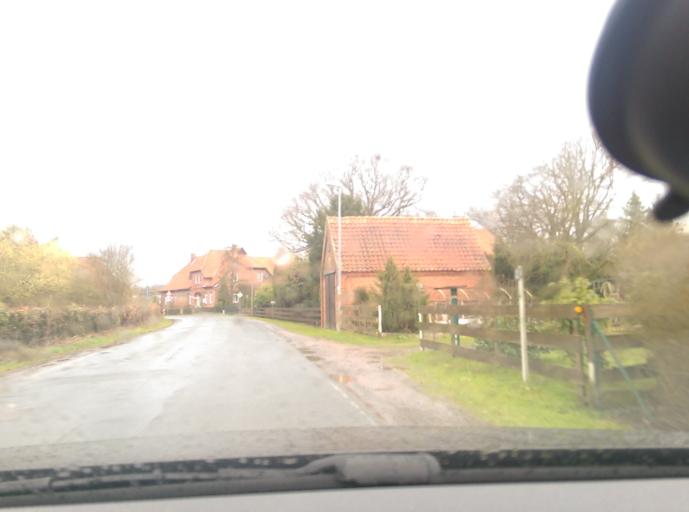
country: DE
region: Lower Saxony
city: Schwarmstedt
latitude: 52.6338
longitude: 9.6072
